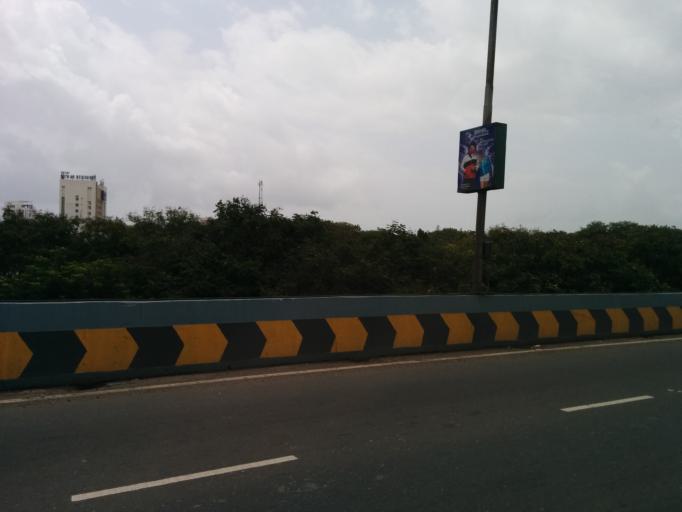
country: IN
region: Maharashtra
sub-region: Thane
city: Thane
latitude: 19.2034
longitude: 72.9675
